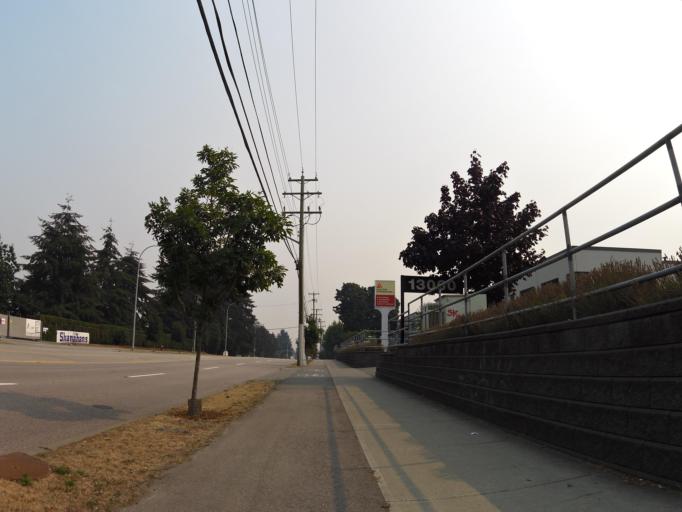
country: CA
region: British Columbia
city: Delta
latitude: 49.1481
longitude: -122.8606
